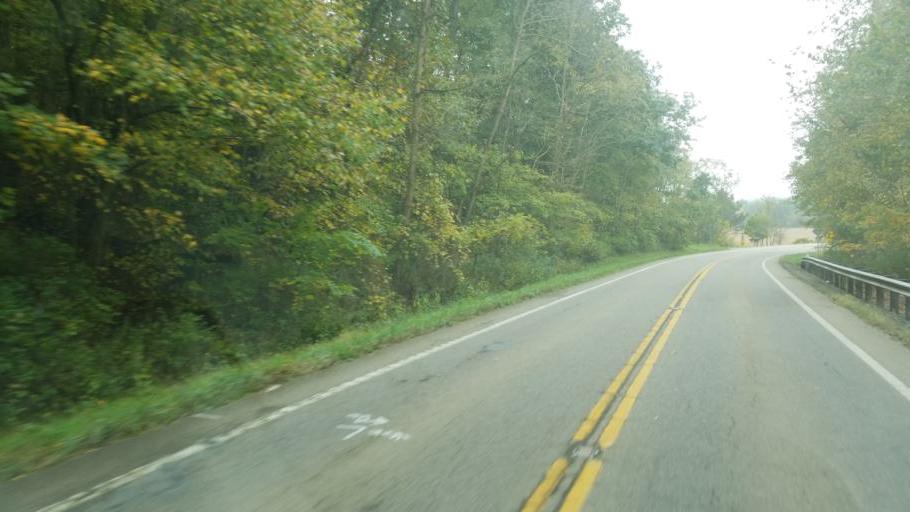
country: US
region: Ohio
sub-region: Tuscarawas County
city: Strasburg
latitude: 40.6546
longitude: -81.4668
